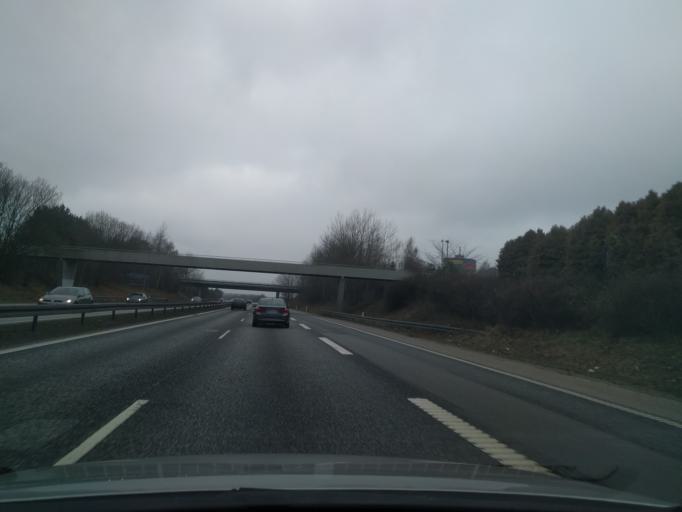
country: DK
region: Zealand
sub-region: Soro Kommune
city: Soro
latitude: 55.4538
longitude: 11.5501
